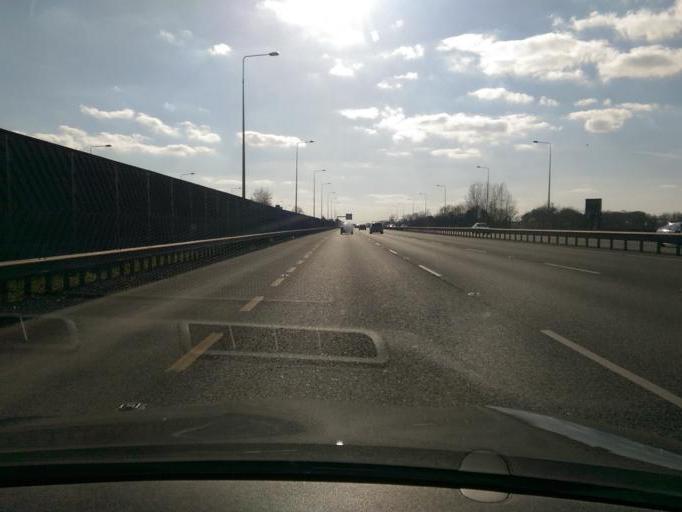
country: IE
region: Leinster
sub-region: Kildare
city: Kill
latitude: 53.2460
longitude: -6.6012
